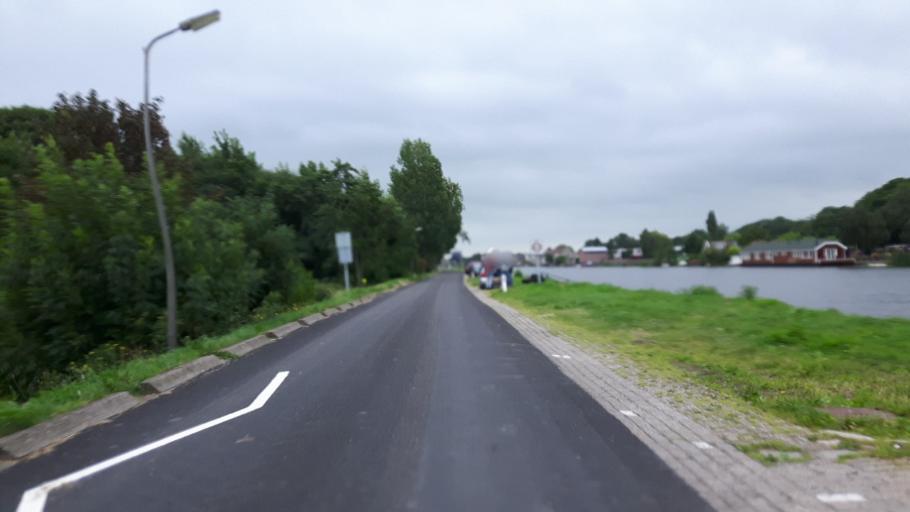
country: NL
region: South Holland
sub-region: Bodegraven-Reeuwijk
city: Bodegraven
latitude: 52.1100
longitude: 4.7169
